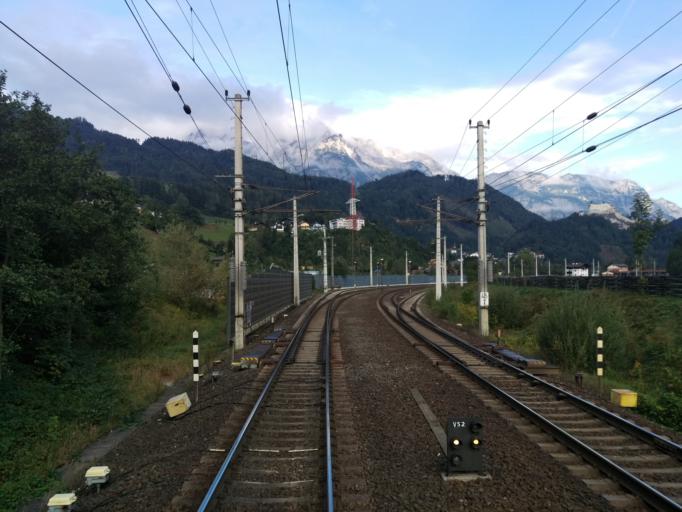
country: AT
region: Salzburg
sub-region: Politischer Bezirk Sankt Johann im Pongau
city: Pfarrwerfen
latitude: 47.4687
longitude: 13.1975
